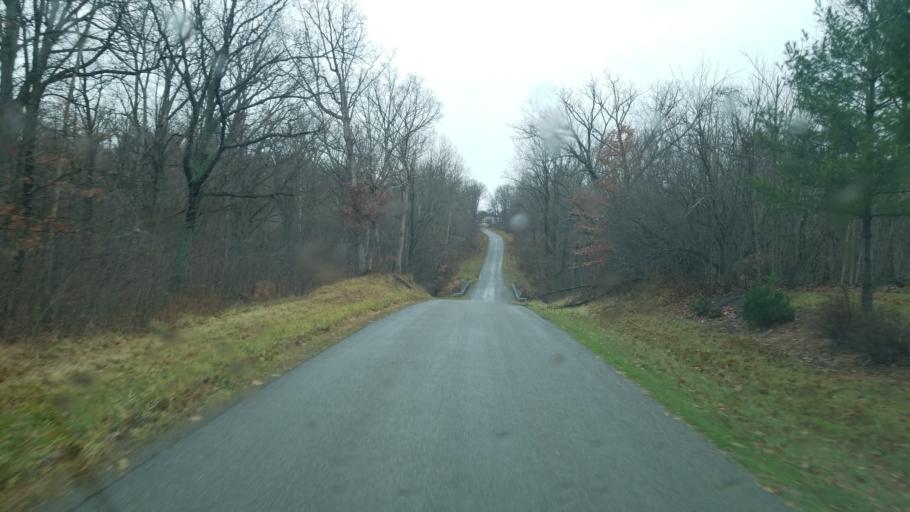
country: US
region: Ohio
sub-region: Logan County
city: Northwood
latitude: 40.4704
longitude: -83.6550
